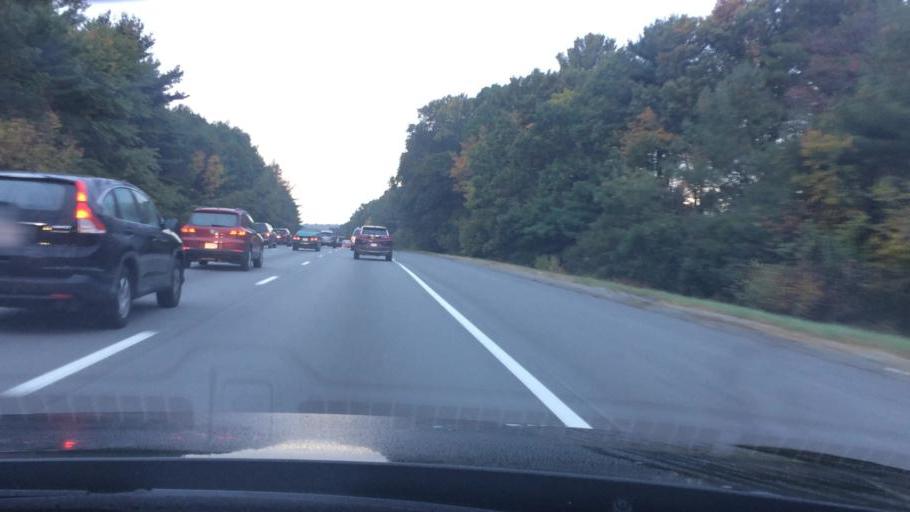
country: US
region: Massachusetts
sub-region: Essex County
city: Lawrence
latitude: 42.6701
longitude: -71.1857
